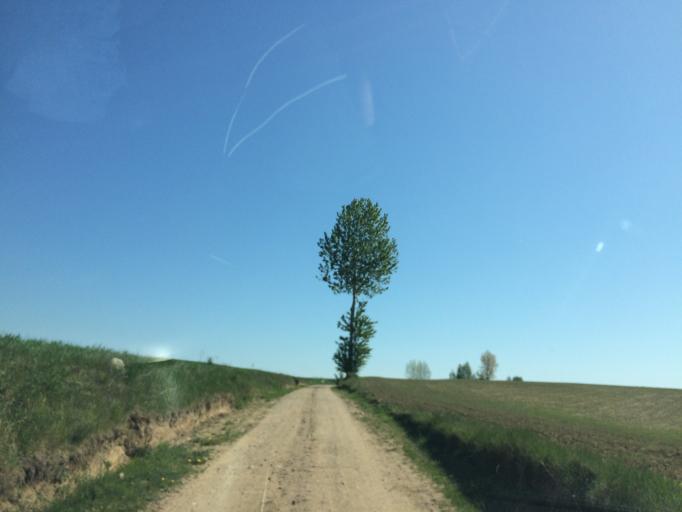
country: PL
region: Warmian-Masurian Voivodeship
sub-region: Powiat nowomiejski
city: Nowe Miasto Lubawskie
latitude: 53.4889
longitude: 19.4985
